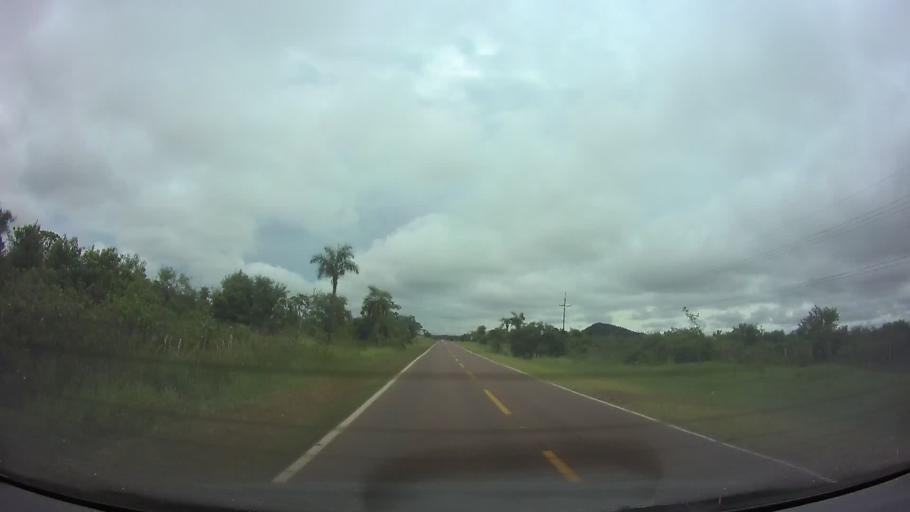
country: PY
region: Paraguari
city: Carapegua
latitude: -25.8203
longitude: -57.1699
